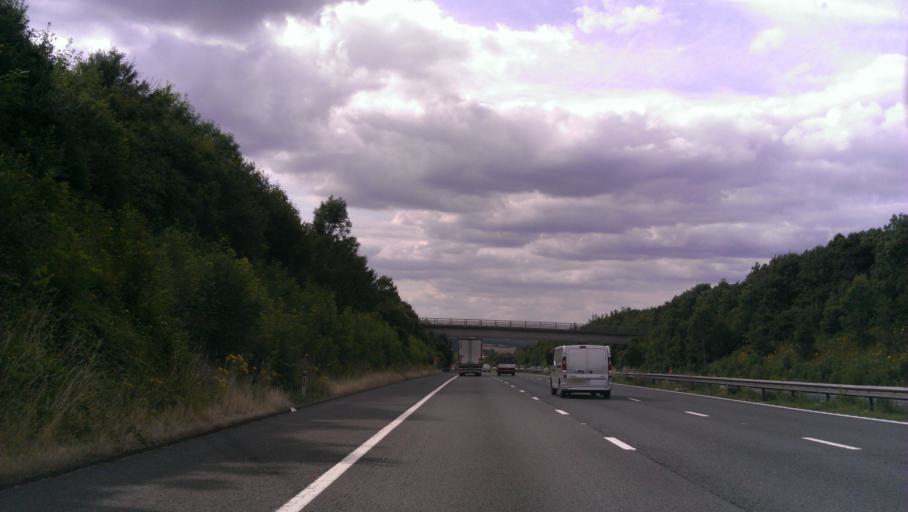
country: GB
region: England
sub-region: Kent
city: Eynsford
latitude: 51.3710
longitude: 0.2535
